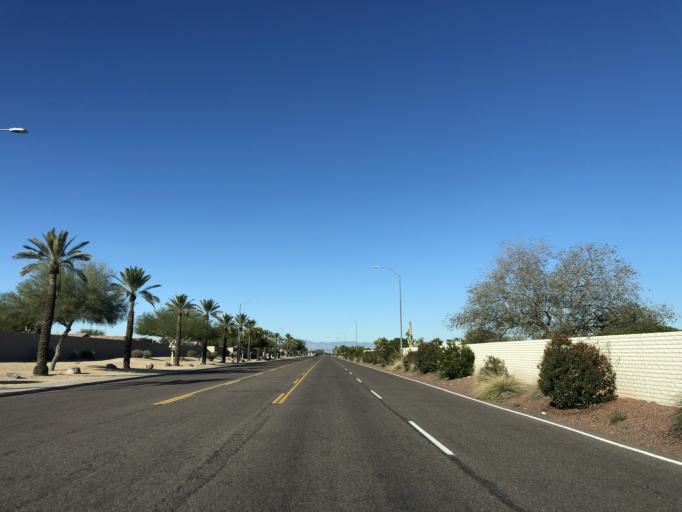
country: US
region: Arizona
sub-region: Maricopa County
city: Sun City West
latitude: 33.6613
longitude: -112.2900
